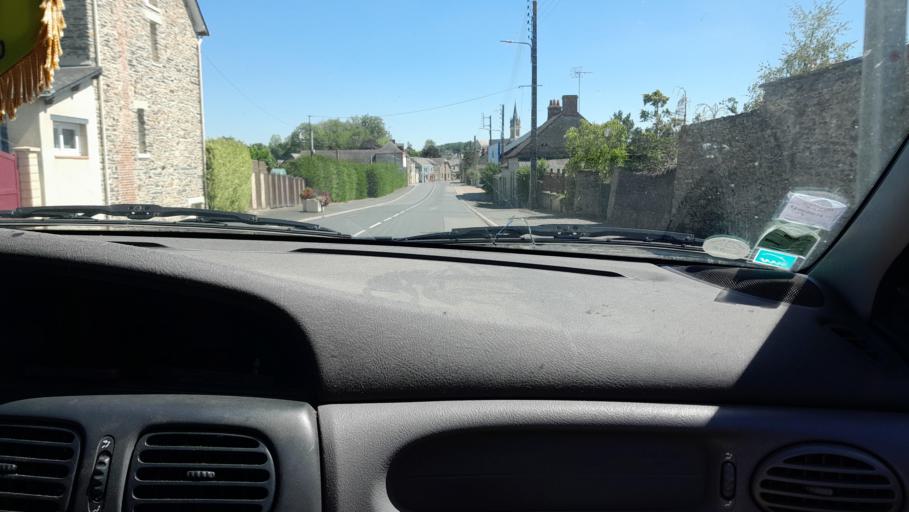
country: FR
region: Pays de la Loire
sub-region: Departement de la Loire-Atlantique
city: Saint-Mars-la-Jaille
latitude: 47.6263
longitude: -1.1997
